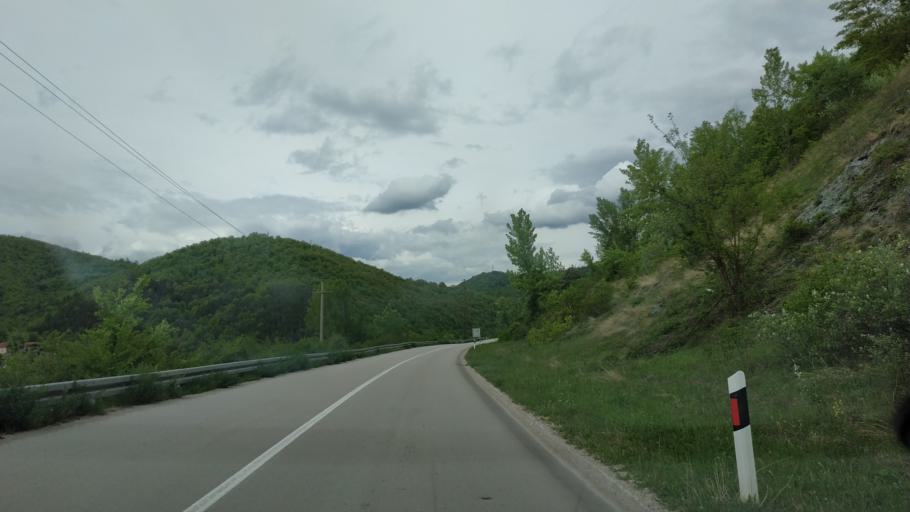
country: RS
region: Central Serbia
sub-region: Nisavski Okrug
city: Aleksinac
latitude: 43.6497
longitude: 21.7137
